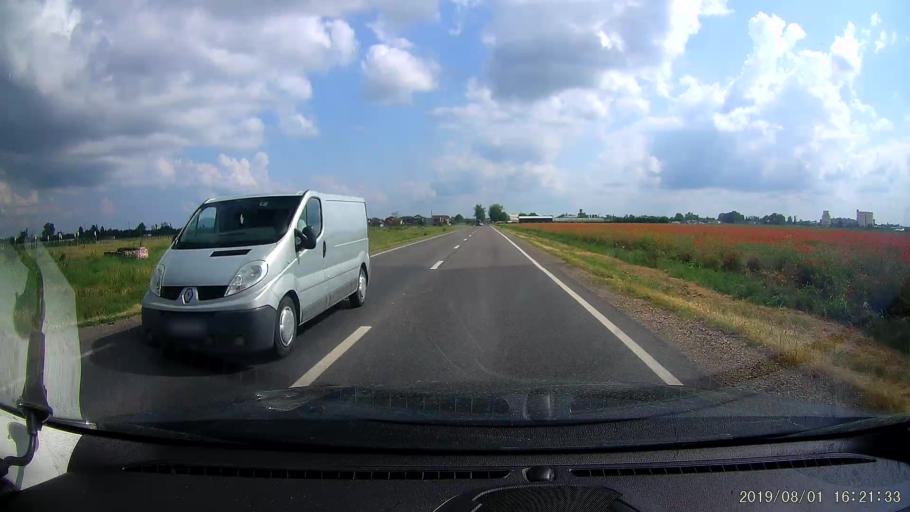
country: RO
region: Calarasi
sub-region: Municipiul Calarasi
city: Calarasi
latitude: 44.2160
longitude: 27.3399
